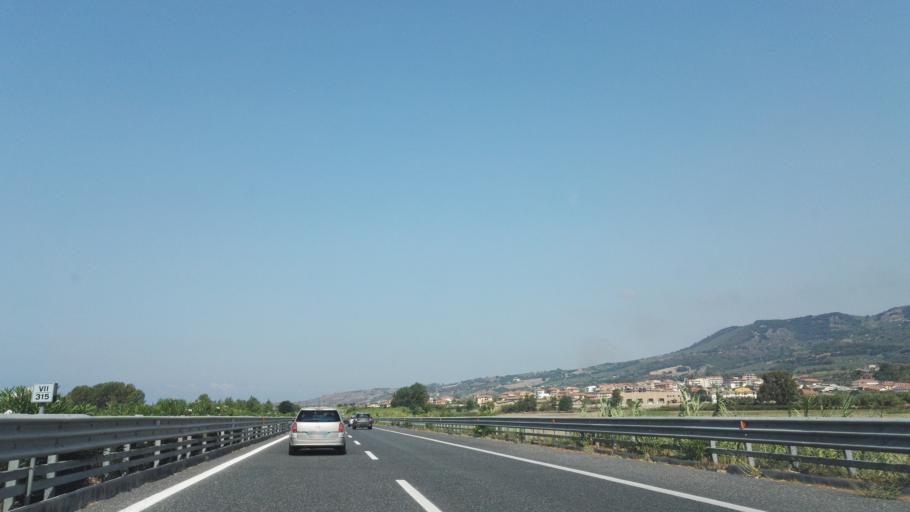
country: IT
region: Calabria
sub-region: Provincia di Catanzaro
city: Santa Eufemia Lamezia
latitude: 38.9348
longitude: 16.2185
